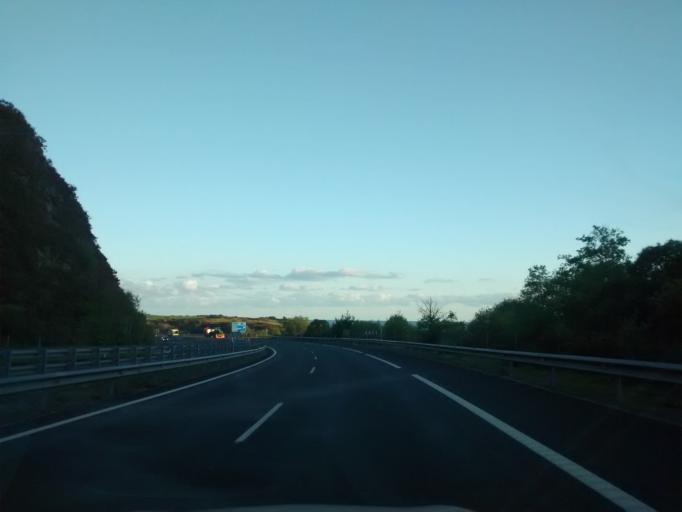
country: ES
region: Asturias
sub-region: Province of Asturias
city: Llanes
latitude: 43.4396
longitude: -4.8725
